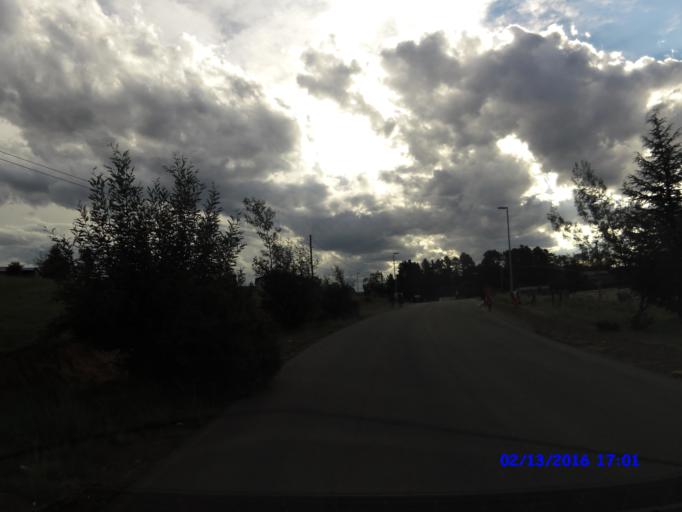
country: LS
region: Qacha's Nek
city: Qacha's Nek
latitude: -30.1167
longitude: 28.6868
